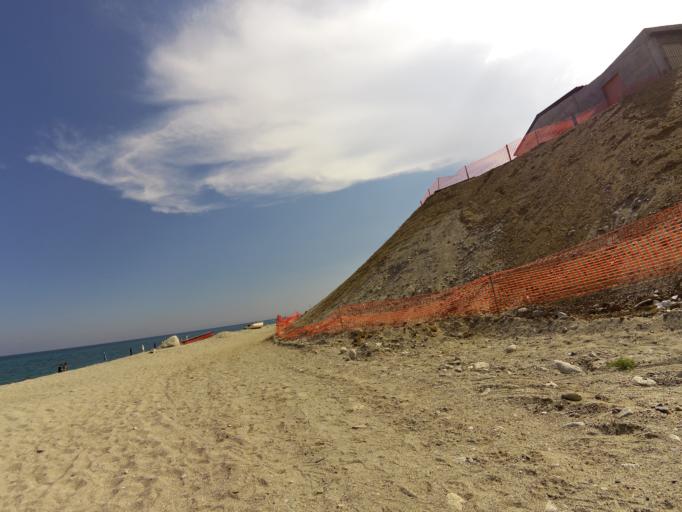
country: IT
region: Calabria
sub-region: Provincia di Reggio Calabria
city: Monasterace Marina
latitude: 38.4444
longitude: 16.5788
